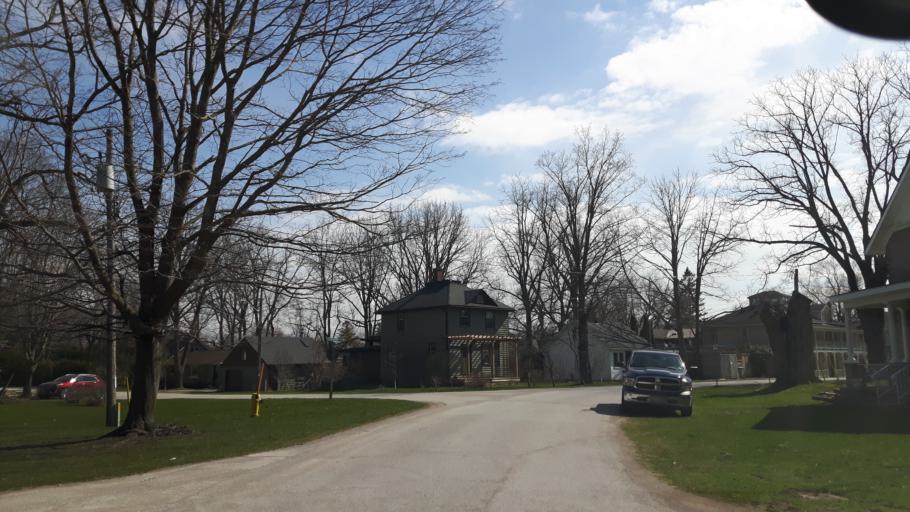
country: CA
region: Ontario
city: Bluewater
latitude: 43.5663
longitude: -81.7009
